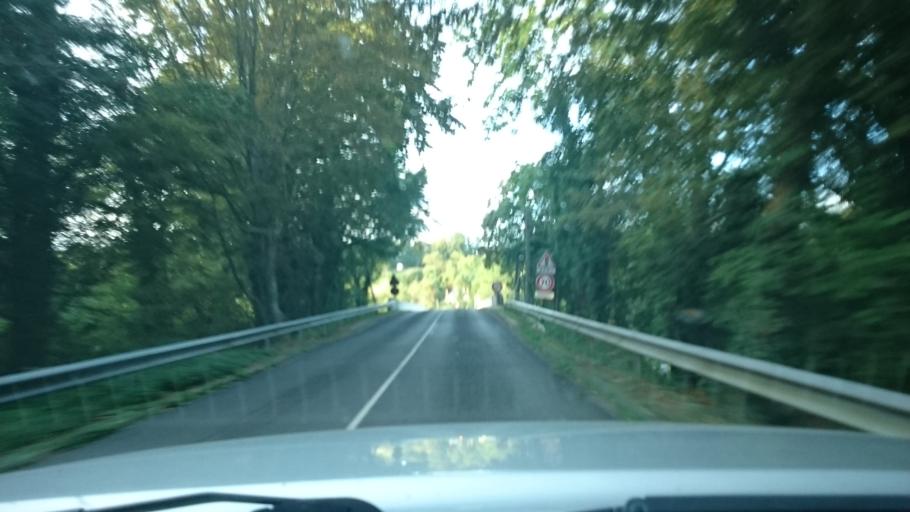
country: FR
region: Ile-de-France
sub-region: Departement de Seine-et-Marne
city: Samois-sur-Seine
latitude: 48.4847
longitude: 2.7515
